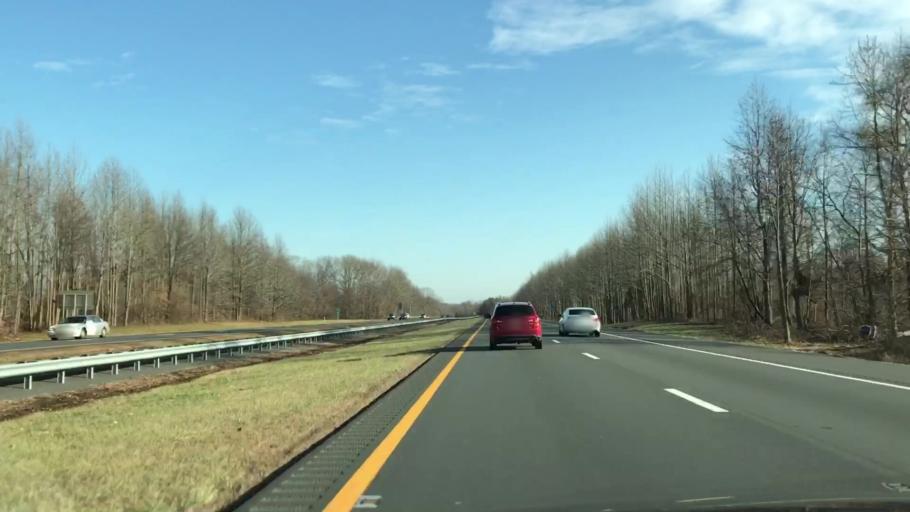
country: US
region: New Jersey
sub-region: Monmouth County
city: Shrewsbury
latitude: 40.1802
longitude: -74.5540
